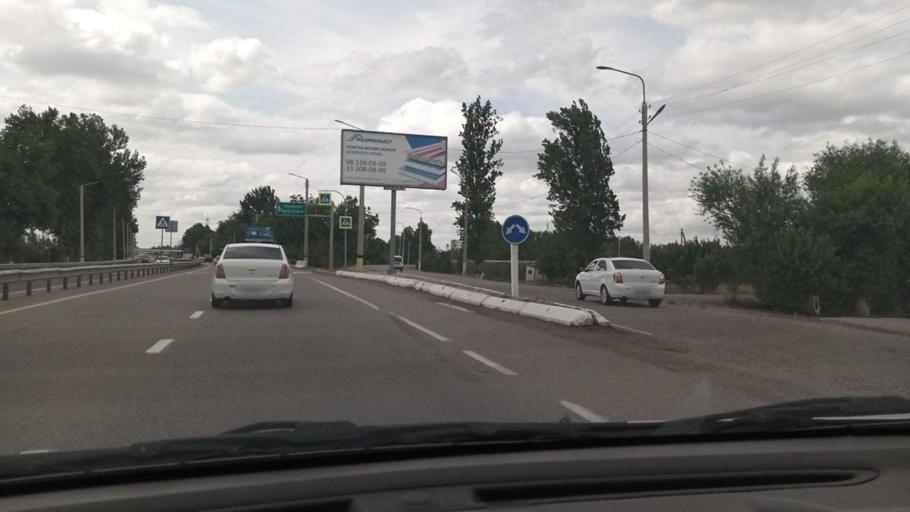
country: UZ
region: Toshkent Shahri
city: Bektemir
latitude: 41.2407
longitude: 69.4009
